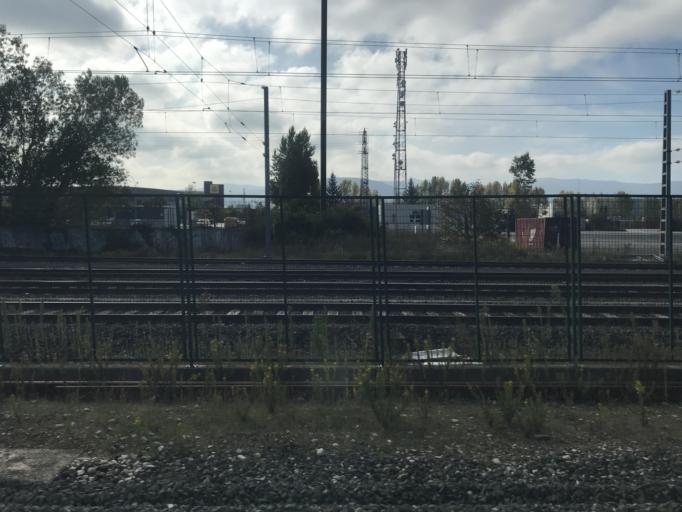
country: ES
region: Basque Country
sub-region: Provincia de Alava
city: Gasteiz / Vitoria
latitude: 42.8525
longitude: -2.7364
